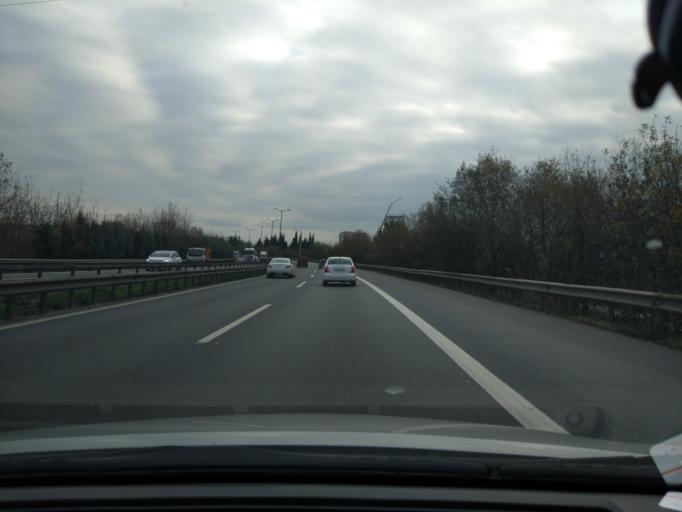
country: TR
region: Kocaeli
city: Kosekoy
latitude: 40.7704
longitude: 29.9871
